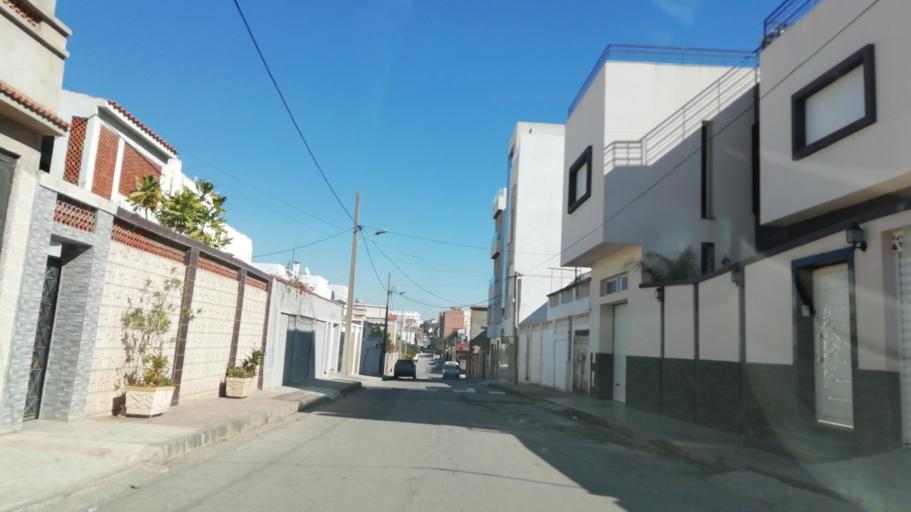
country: DZ
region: Oran
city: Oran
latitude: 35.6925
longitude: -0.6172
